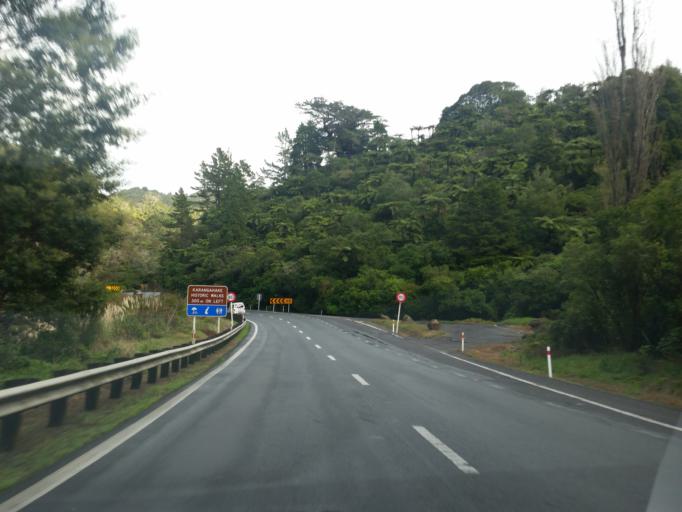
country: NZ
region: Waikato
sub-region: Hauraki District
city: Paeroa
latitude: -37.4225
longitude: 175.7267
